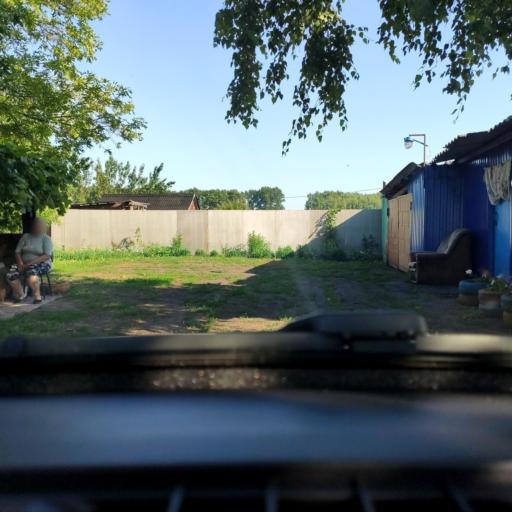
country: RU
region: Voronezj
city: Panino
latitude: 51.5740
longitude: 39.9162
